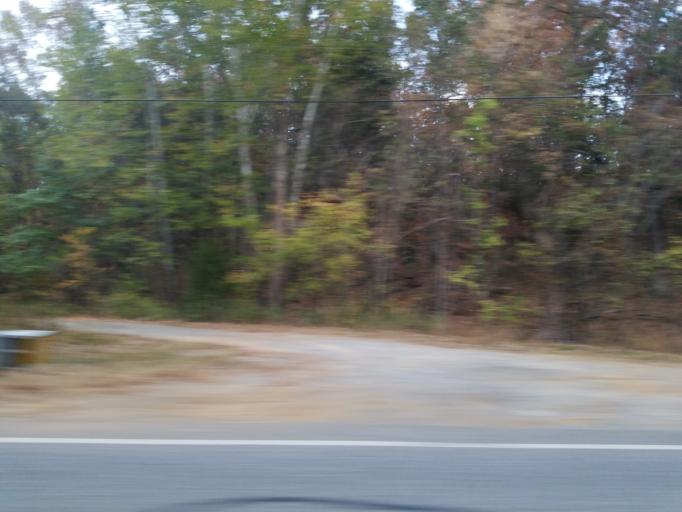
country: US
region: Georgia
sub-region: Murray County
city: Chatsworth
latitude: 34.5897
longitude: -84.6820
